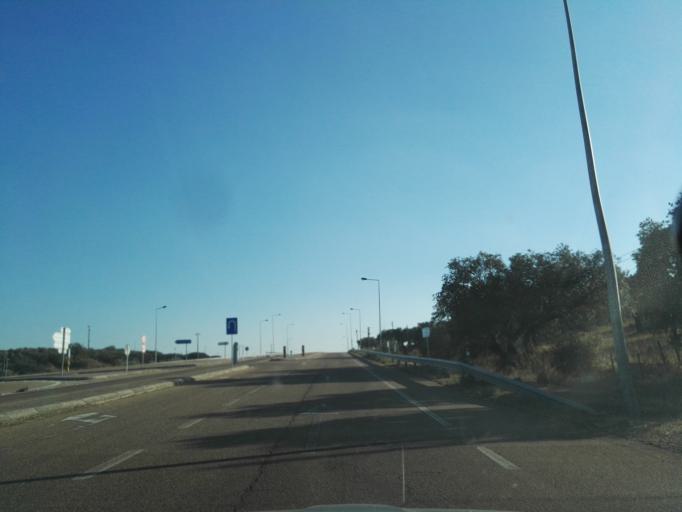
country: PT
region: Portalegre
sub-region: Elvas
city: Elvas
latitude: 38.9098
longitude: -7.1803
